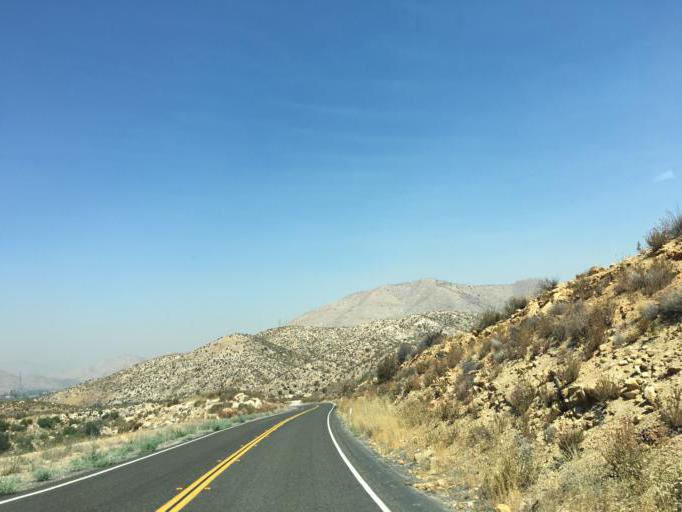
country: US
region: California
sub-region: Los Angeles County
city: Vincent
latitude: 34.4278
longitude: -118.1110
